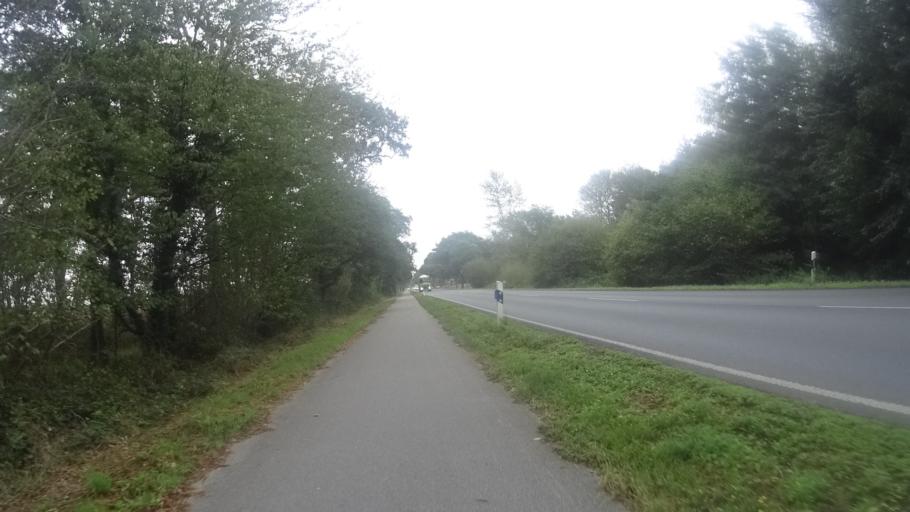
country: DE
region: North Rhine-Westphalia
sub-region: Regierungsbezirk Dusseldorf
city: Issum
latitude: 51.5251
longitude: 6.3823
